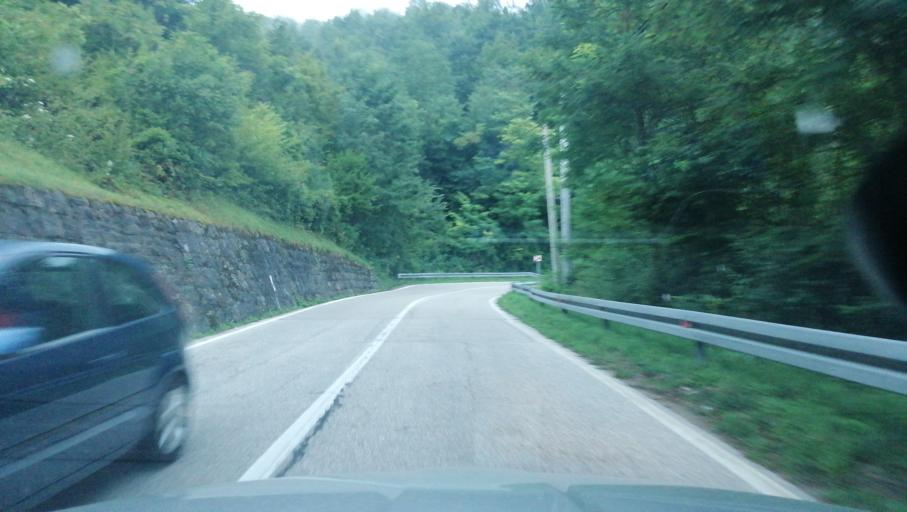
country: BA
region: Federation of Bosnia and Herzegovina
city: Jablanica
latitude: 43.7062
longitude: 17.7164
